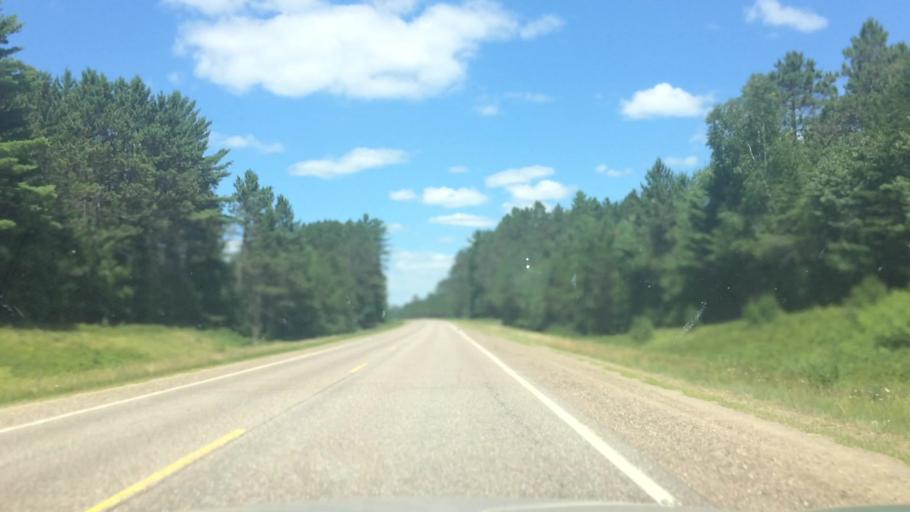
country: US
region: Wisconsin
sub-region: Vilas County
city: Lac du Flambeau
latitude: 46.0884
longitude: -89.6452
